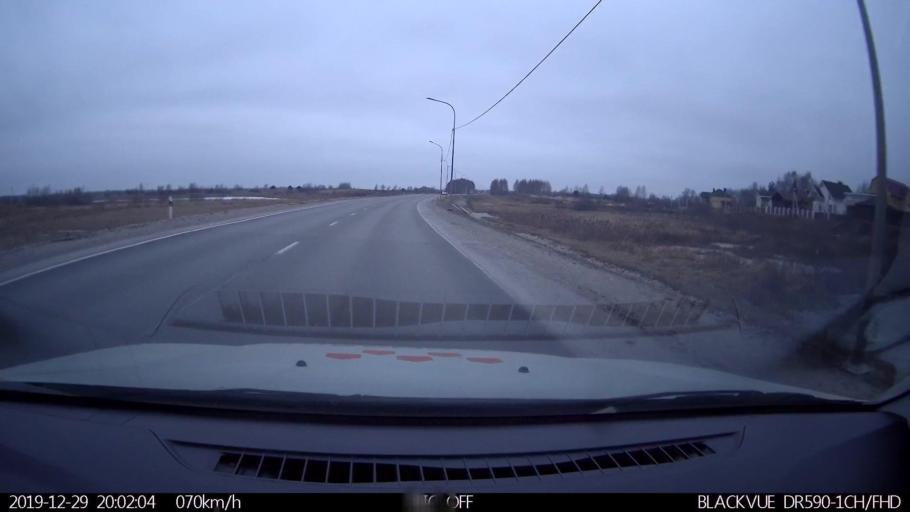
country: RU
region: Nizjnij Novgorod
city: Bor
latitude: 56.3627
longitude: 44.0343
